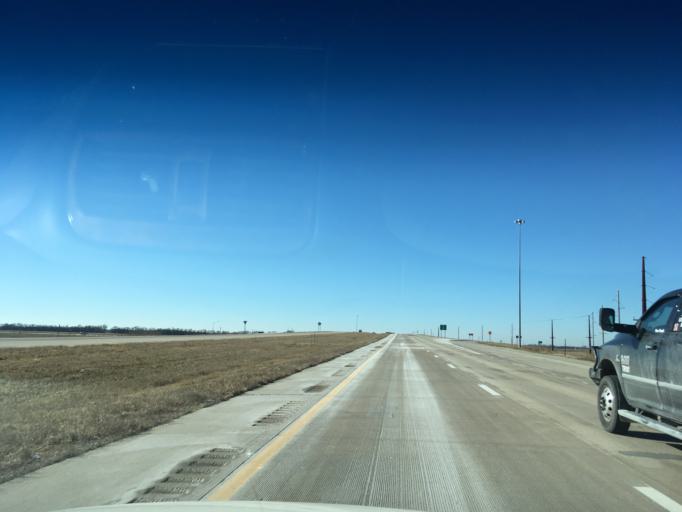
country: US
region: Kansas
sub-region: Reno County
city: Hutchinson
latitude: 38.0287
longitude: -97.8616
